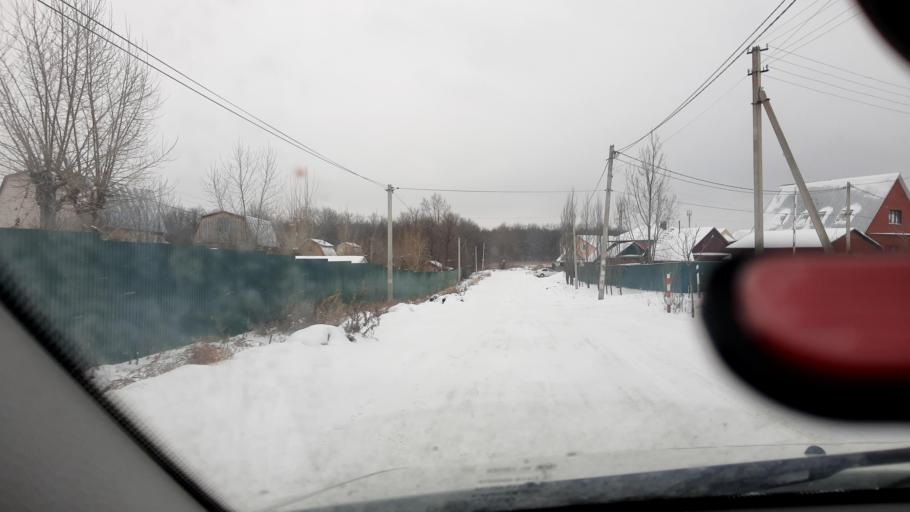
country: RU
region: Bashkortostan
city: Kabakovo
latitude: 54.6296
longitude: 56.0811
